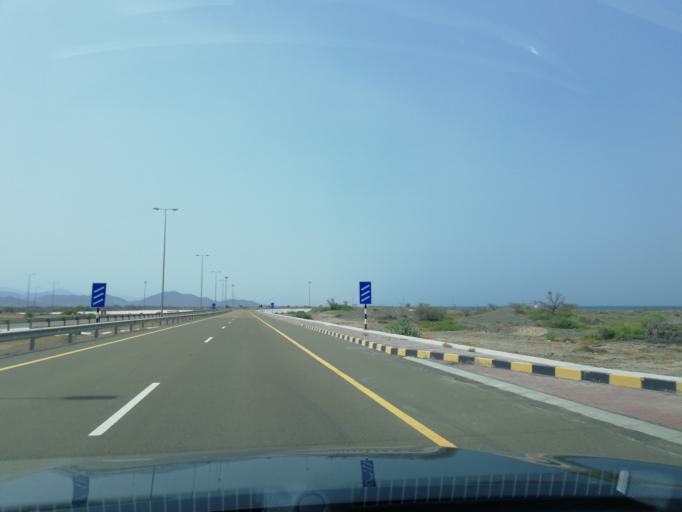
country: OM
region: Al Batinah
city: Shinas
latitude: 24.9144
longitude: 56.3901
